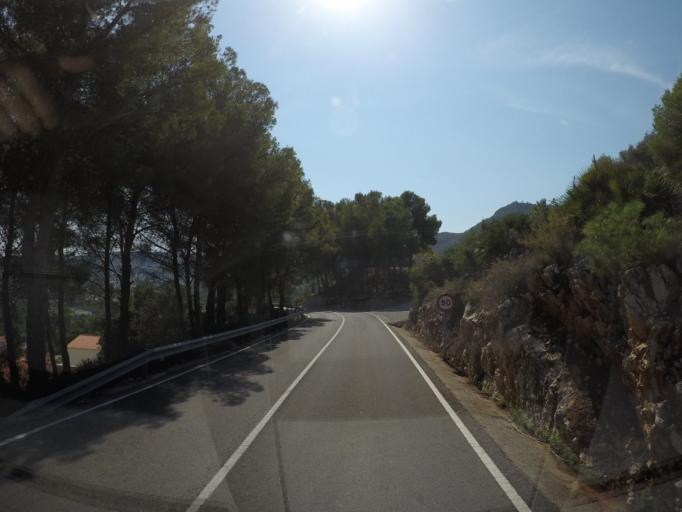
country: ES
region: Valencia
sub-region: Provincia de Alicante
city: Orba
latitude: 38.7843
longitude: -0.0813
